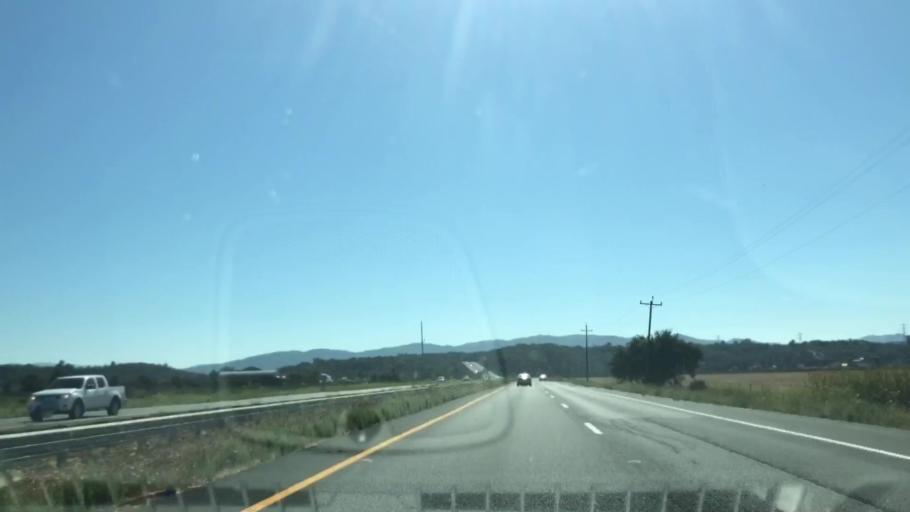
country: US
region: California
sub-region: Marin County
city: Black Point-Green Point
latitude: 38.1231
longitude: -122.4950
